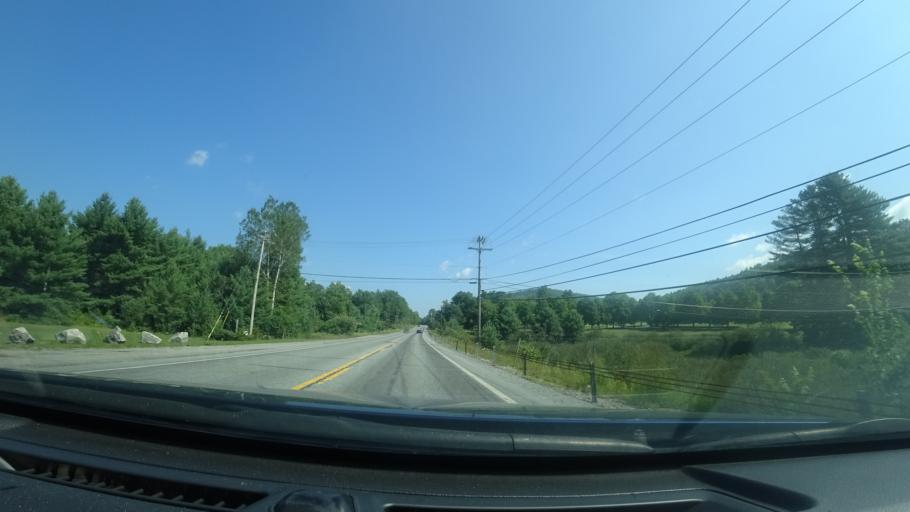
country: US
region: New York
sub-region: Warren County
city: Warrensburg
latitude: 43.6301
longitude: -73.7988
